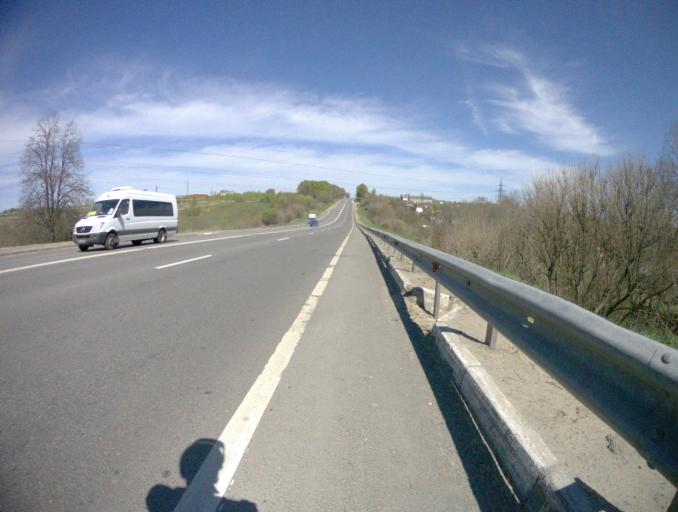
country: RU
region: Vladimir
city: Bogolyubovo
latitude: 56.1807
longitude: 40.5076
